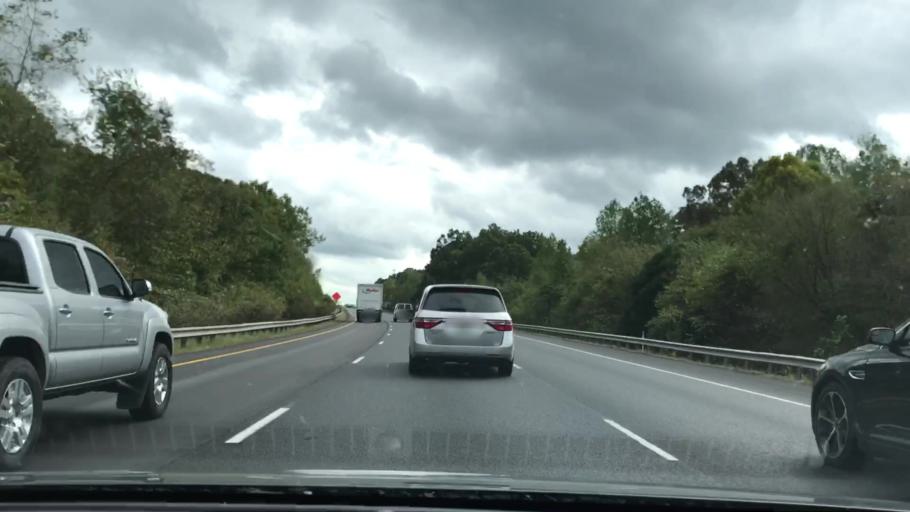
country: US
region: Tennessee
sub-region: Robertson County
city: Coopertown
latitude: 36.3589
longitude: -86.9489
